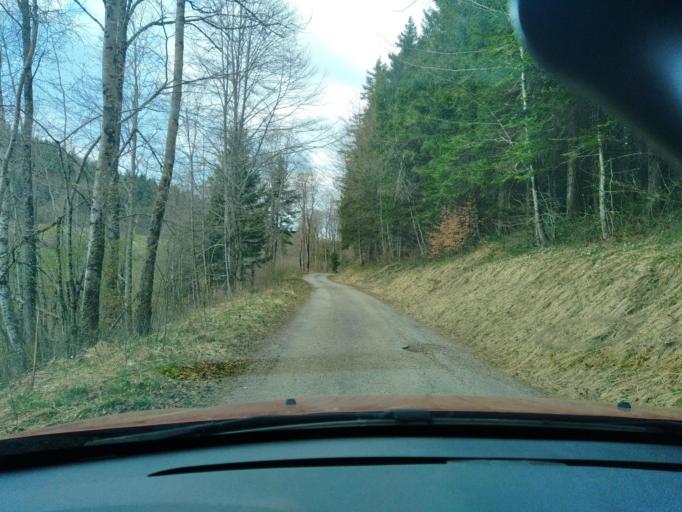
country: FR
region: Franche-Comte
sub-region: Departement du Jura
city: Moirans-en-Montagne
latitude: 46.4571
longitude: 5.7604
